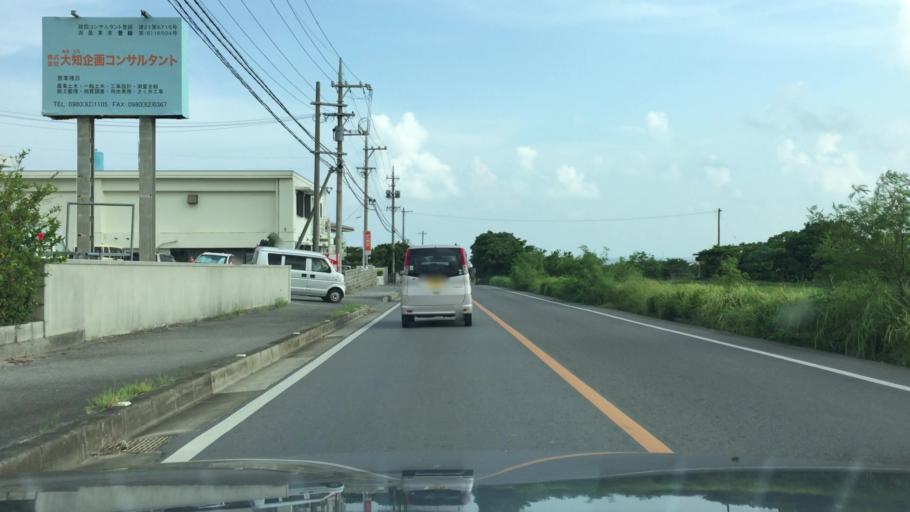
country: JP
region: Okinawa
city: Ishigaki
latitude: 24.3558
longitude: 124.1740
